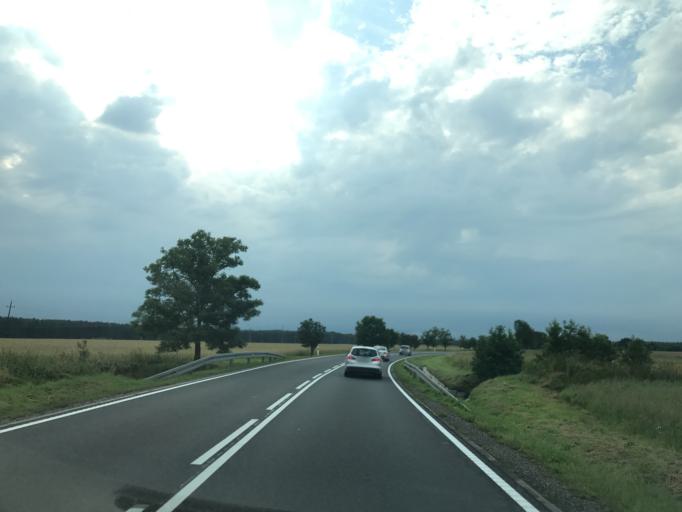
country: PL
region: Pomeranian Voivodeship
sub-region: Powiat czluchowski
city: Rzeczenica
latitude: 53.7417
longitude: 17.1799
